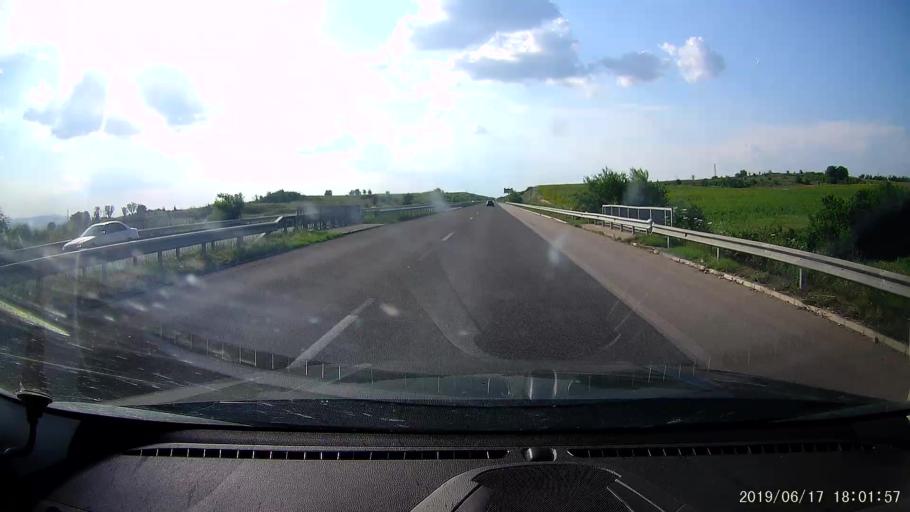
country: BG
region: Khaskovo
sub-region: Obshtina Svilengrad
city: Svilengrad
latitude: 41.7512
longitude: 26.2405
